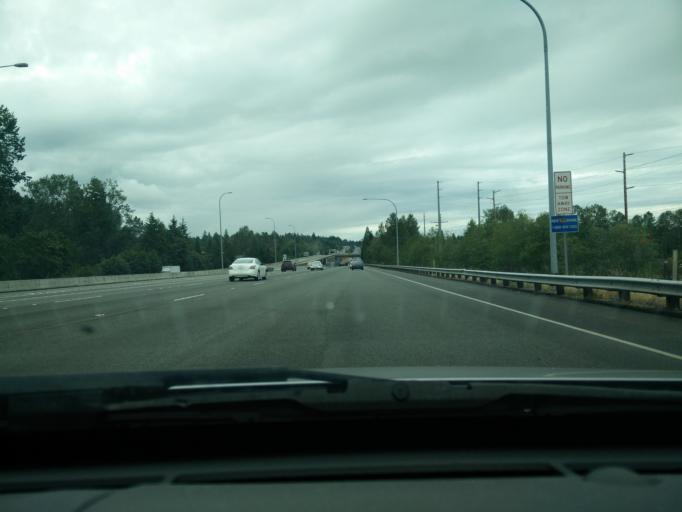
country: US
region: Washington
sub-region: Snohomish County
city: Alderwood Manor
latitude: 47.8159
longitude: -122.2893
